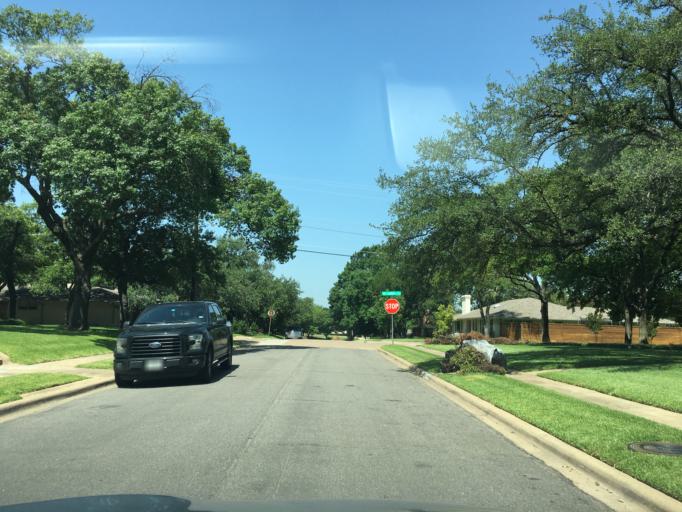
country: US
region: Texas
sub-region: Dallas County
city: University Park
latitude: 32.9041
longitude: -96.7842
